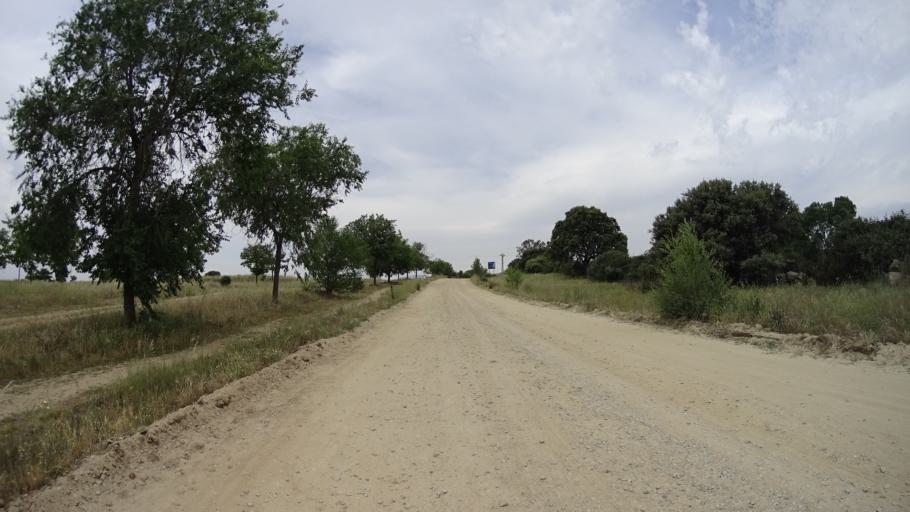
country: ES
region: Madrid
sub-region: Provincia de Madrid
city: Colmenarejo
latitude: 40.5683
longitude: -4.0249
